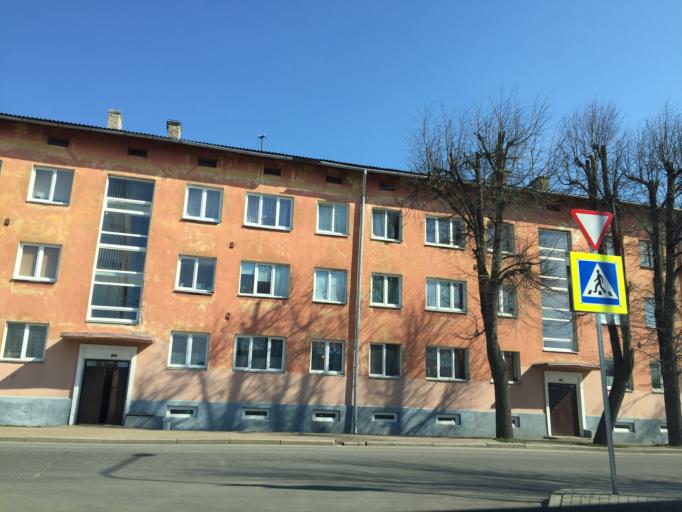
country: EE
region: Ida-Virumaa
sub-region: Narva linn
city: Narva
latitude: 59.3693
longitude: 28.1996
